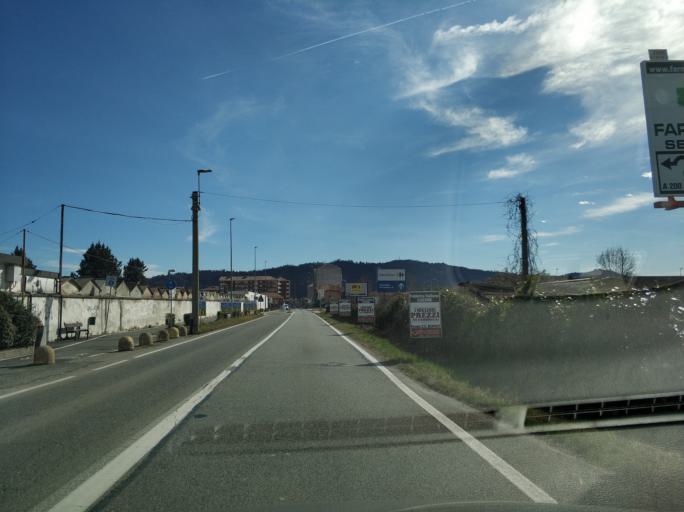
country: IT
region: Piedmont
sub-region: Provincia di Torino
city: Chivasso
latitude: 45.1997
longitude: 7.8898
